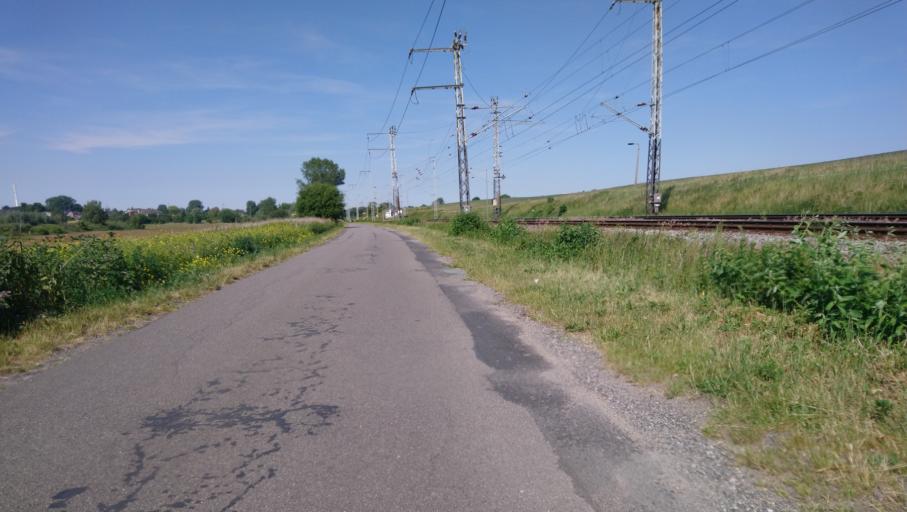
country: DE
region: Mecklenburg-Vorpommern
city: Dierkow-Neu
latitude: 54.0864
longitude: 12.1763
